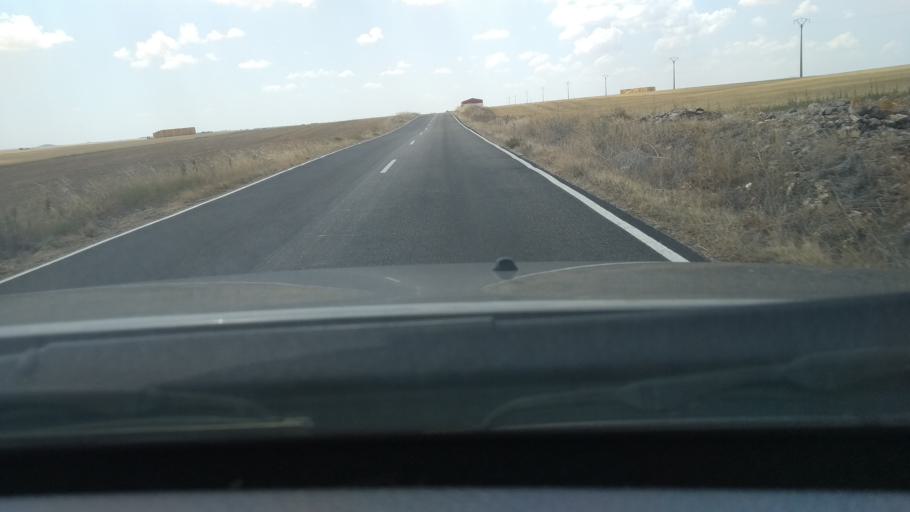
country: ES
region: Castille and Leon
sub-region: Provincia de Burgos
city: Villafruela
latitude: 41.9336
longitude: -3.8826
